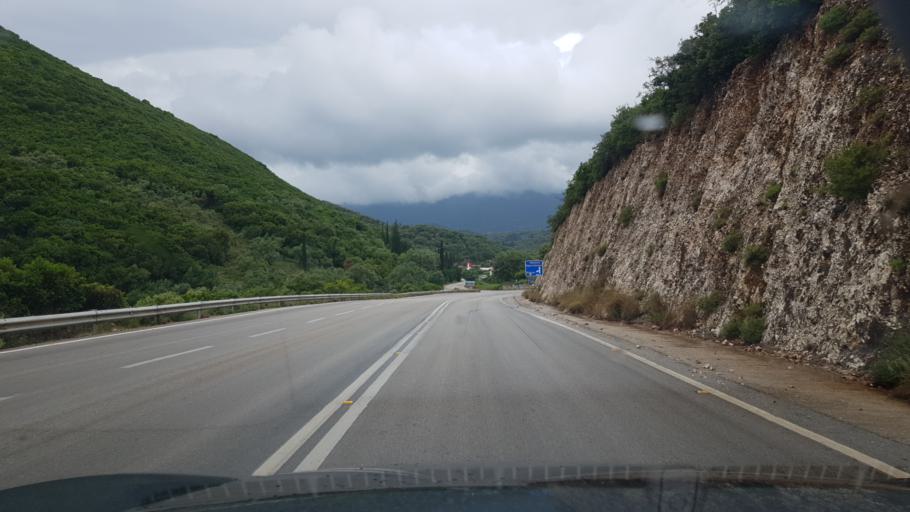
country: GR
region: Ionian Islands
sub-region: Lefkada
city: Nidri
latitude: 38.6330
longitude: 20.6679
